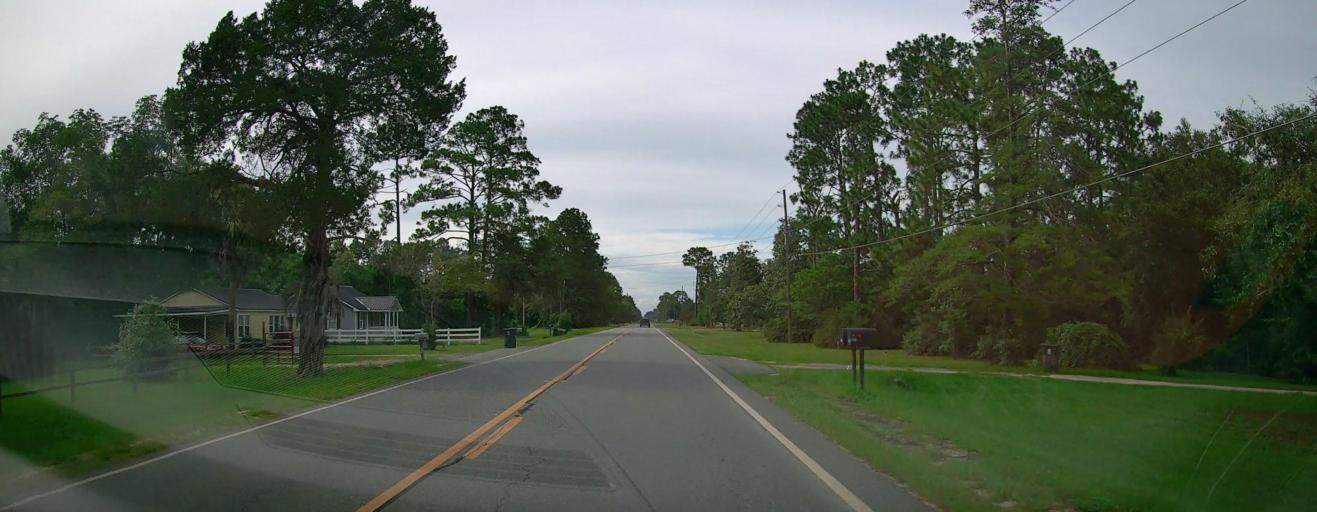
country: US
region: Georgia
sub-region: Wayne County
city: Jesup
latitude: 31.6314
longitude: -81.9015
